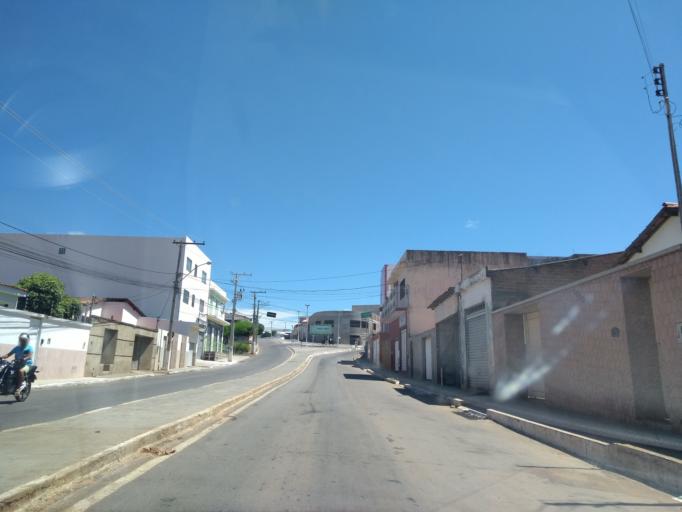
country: BR
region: Bahia
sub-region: Brumado
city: Brumado
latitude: -14.2098
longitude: -41.6787
